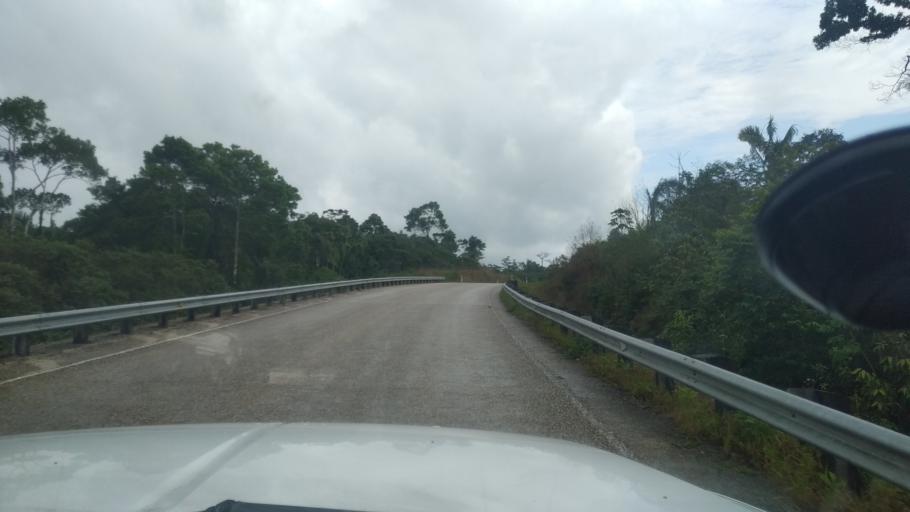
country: GT
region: Peten
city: San Luis
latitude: 16.1960
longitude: -89.1658
